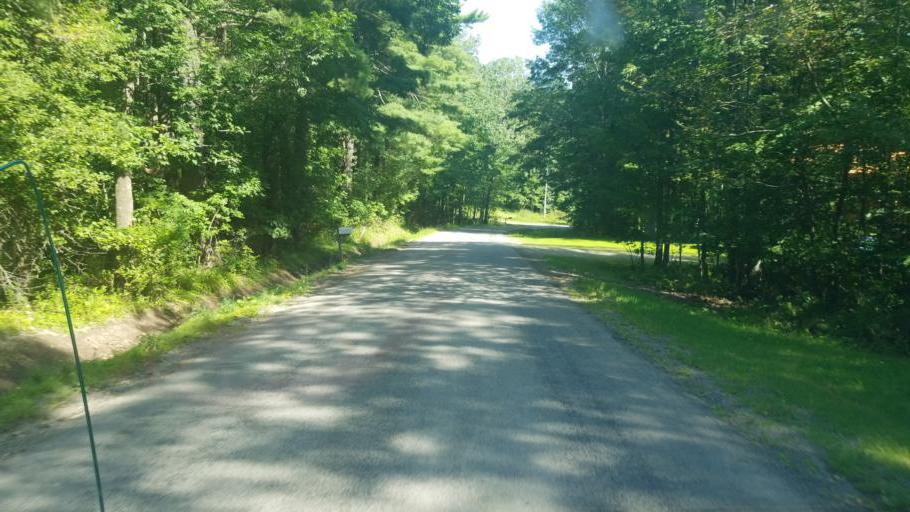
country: US
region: New York
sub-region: Allegany County
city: Wellsville
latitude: 42.0644
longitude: -78.0501
